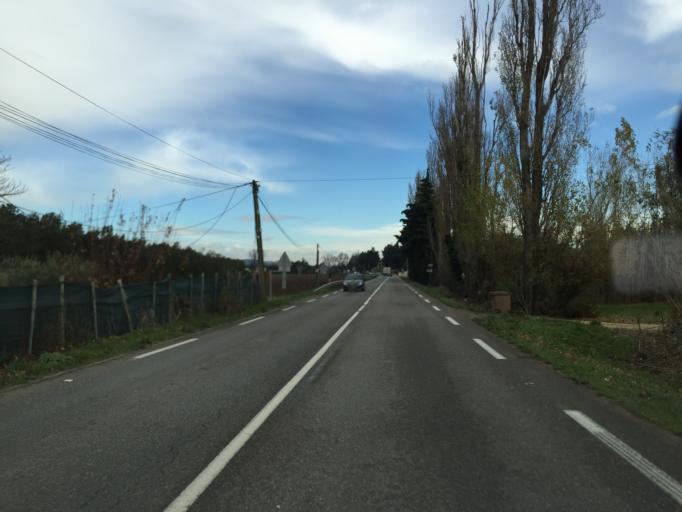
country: FR
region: Provence-Alpes-Cote d'Azur
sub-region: Departement du Vaucluse
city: L'Isle-sur-la-Sorgue
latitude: 43.8742
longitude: 5.0588
